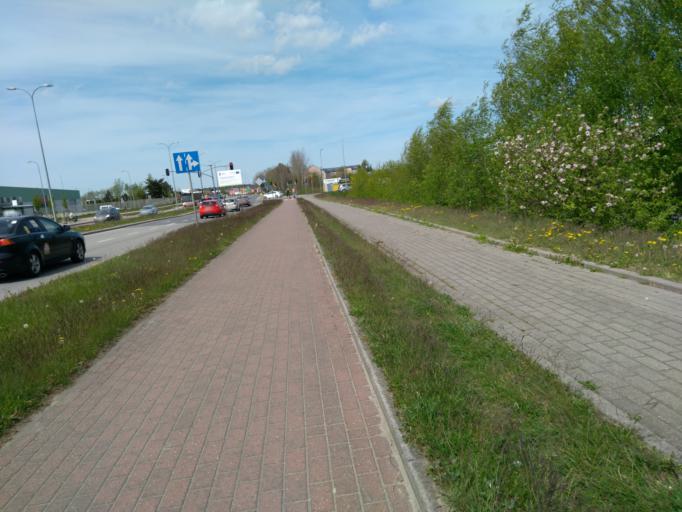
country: PL
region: Pomeranian Voivodeship
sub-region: Gdynia
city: Wielki Kack
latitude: 54.4136
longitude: 18.4809
